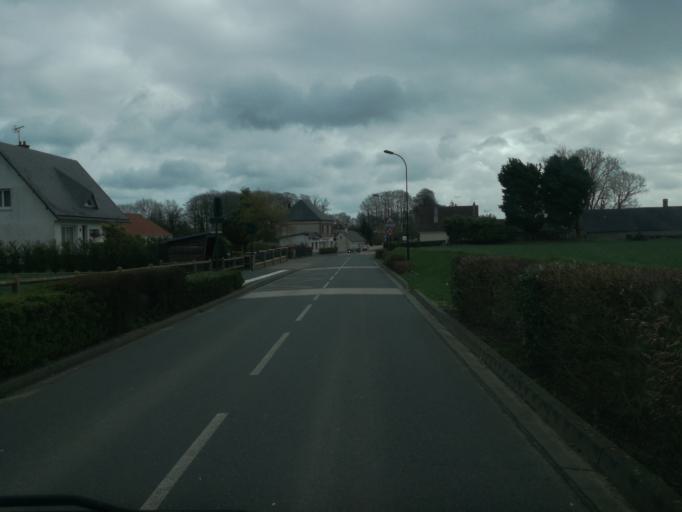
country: FR
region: Haute-Normandie
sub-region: Departement de la Seine-Maritime
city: Yebleron
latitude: 49.6662
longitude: 0.5009
